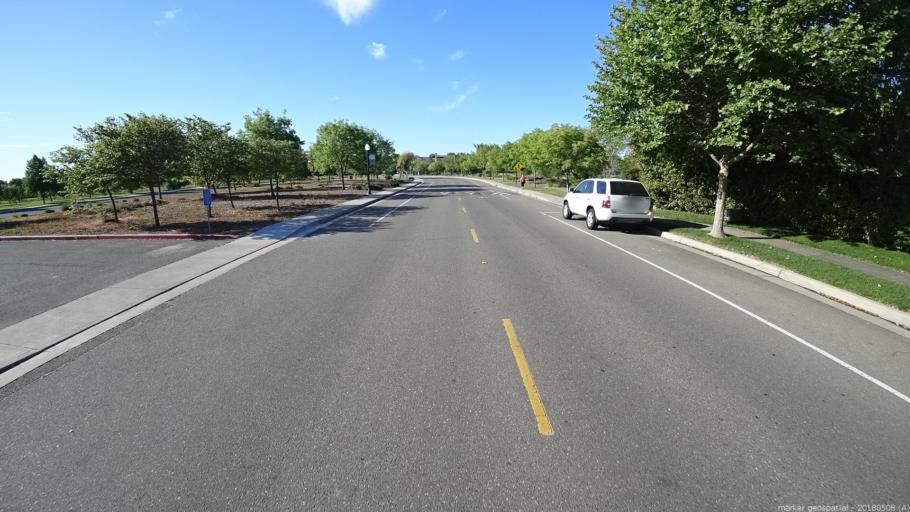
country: US
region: California
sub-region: Sacramento County
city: Elverta
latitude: 38.6750
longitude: -121.5043
